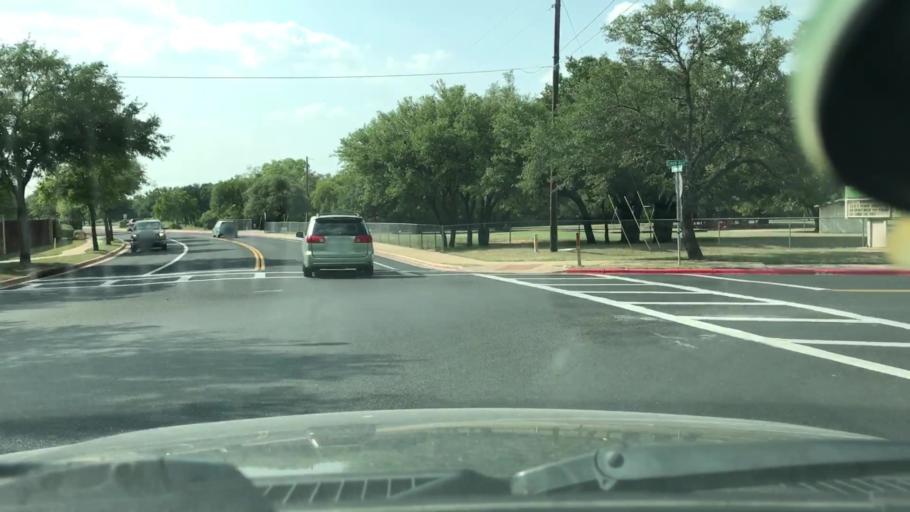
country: US
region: Texas
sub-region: Williamson County
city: Cedar Park
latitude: 30.5396
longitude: -97.8325
